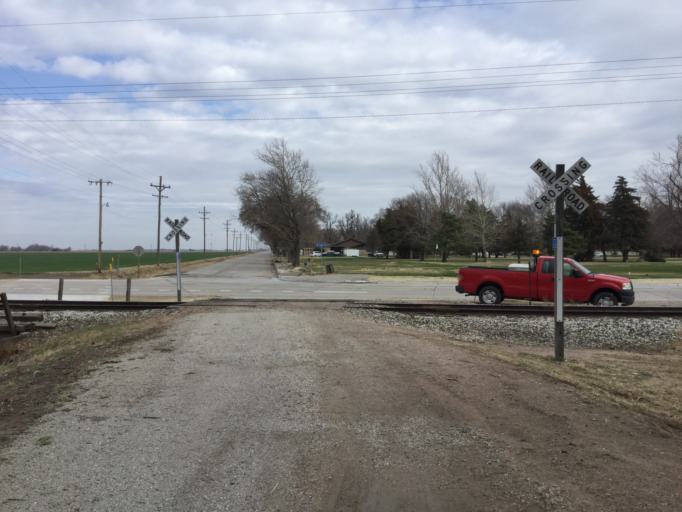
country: US
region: Kansas
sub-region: Barton County
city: Ellinwood
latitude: 38.3553
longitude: -98.5904
